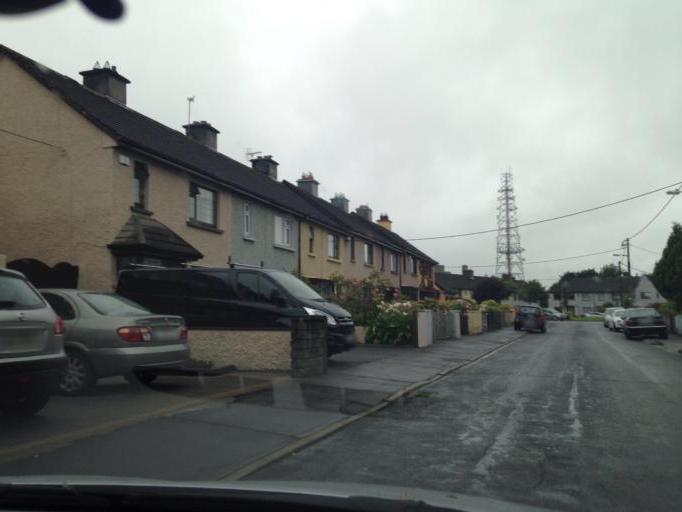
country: IE
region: Connaught
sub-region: County Galway
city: Gaillimh
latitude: 53.2864
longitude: -9.0149
